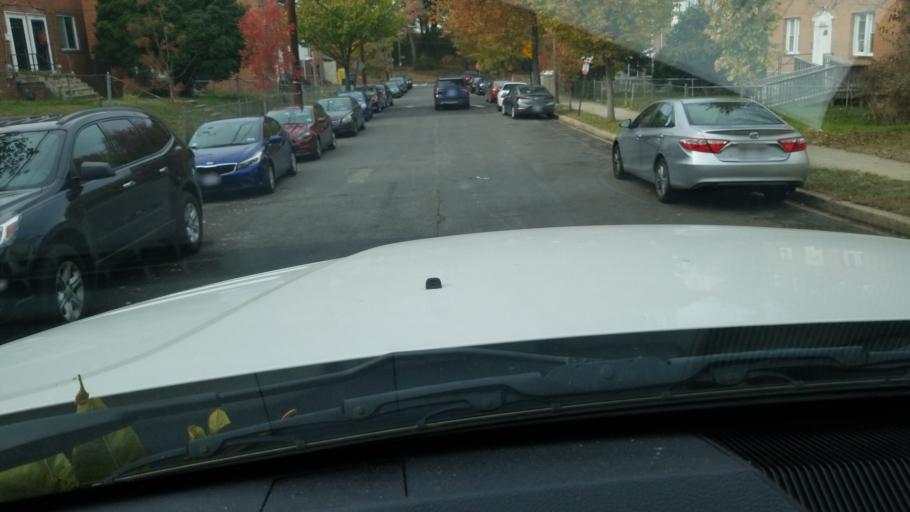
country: US
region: Maryland
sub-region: Prince George's County
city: Fairmount Heights
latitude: 38.8975
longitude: -76.9413
